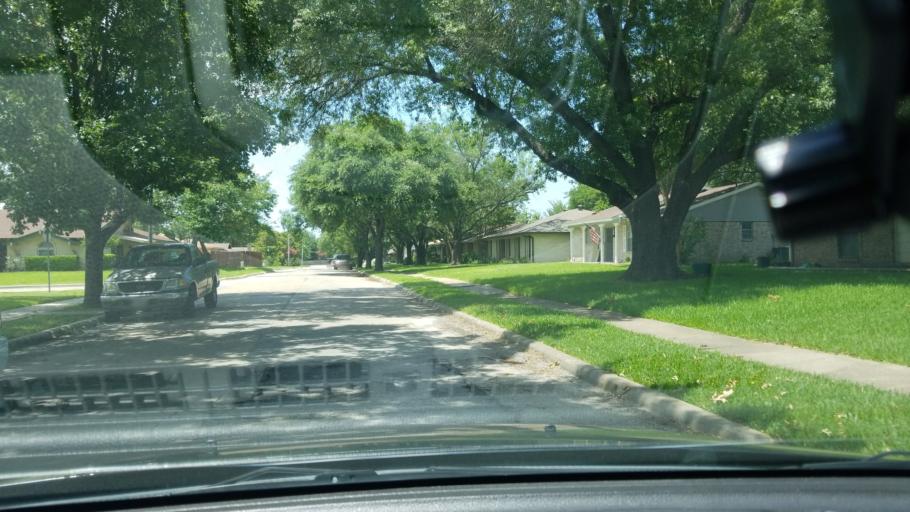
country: US
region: Texas
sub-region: Dallas County
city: Mesquite
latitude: 32.8088
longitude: -96.6494
